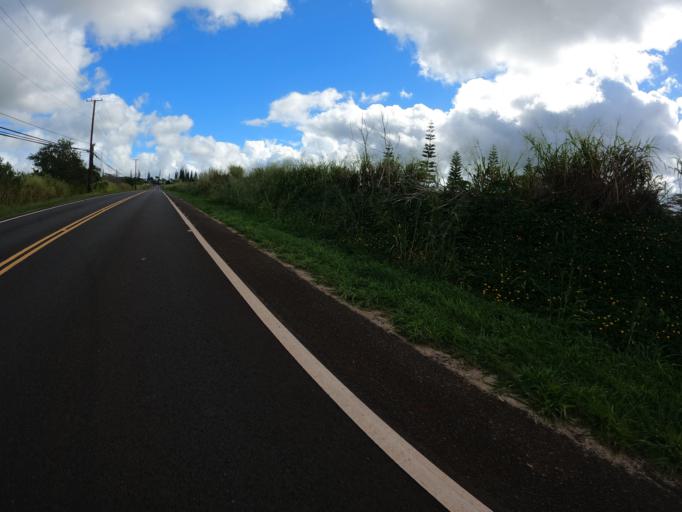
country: US
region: Hawaii
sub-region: Honolulu County
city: Whitmore Village
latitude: 21.5136
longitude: -158.0097
